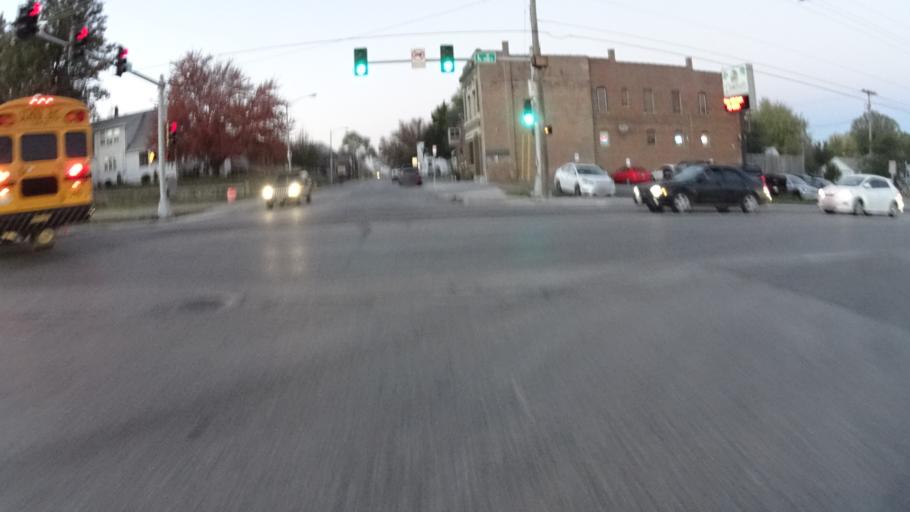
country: US
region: Nebraska
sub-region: Douglas County
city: Omaha
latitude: 41.2121
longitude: -95.9625
